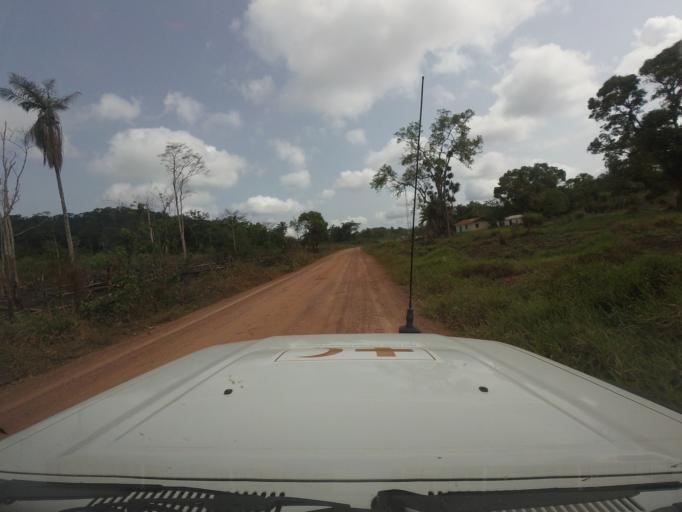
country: LR
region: Bong
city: Gbarnga
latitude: 7.2509
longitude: -9.4353
